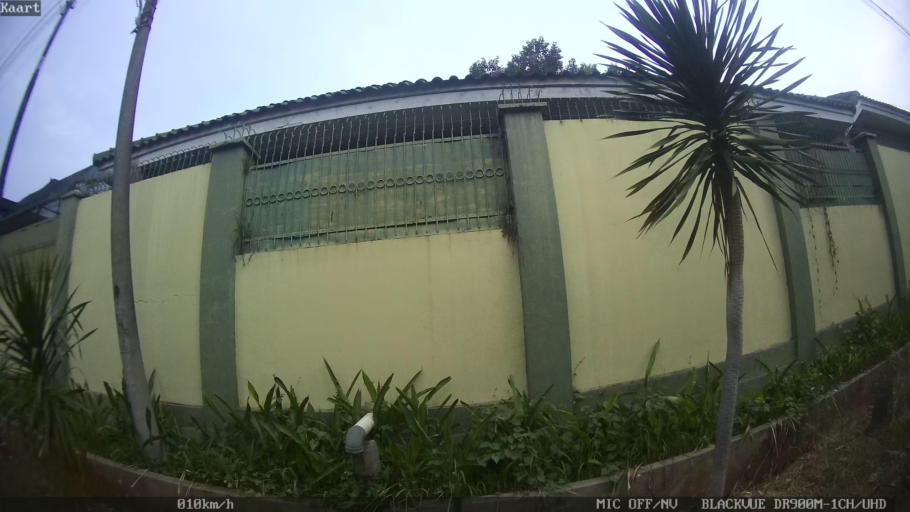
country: ID
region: Lampung
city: Bandarlampung
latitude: -5.4136
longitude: 105.2879
